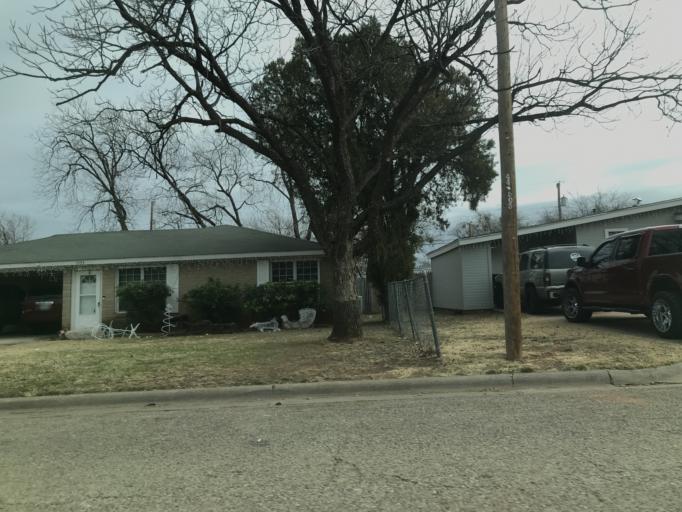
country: US
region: Texas
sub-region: Taylor County
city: Abilene
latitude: 32.4680
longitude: -99.7590
